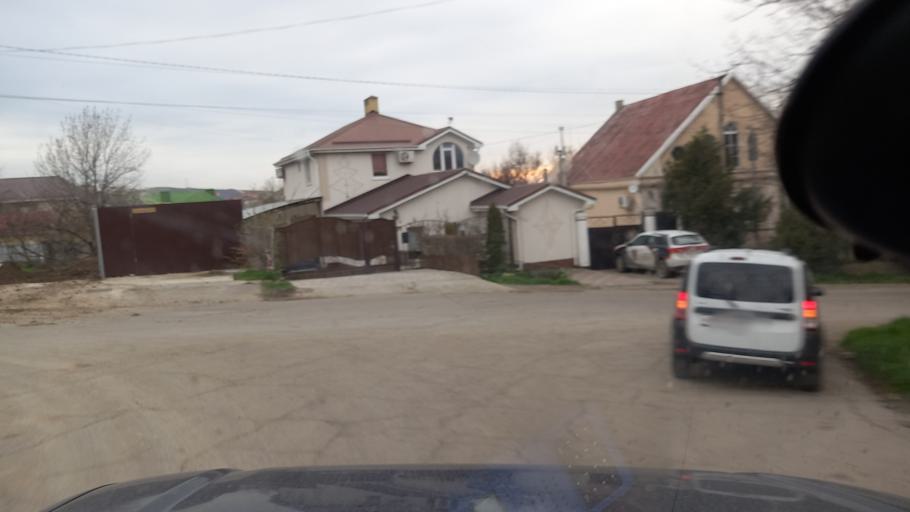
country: RU
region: Krasnodarskiy
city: Anapskaya
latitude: 44.8515
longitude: 37.3634
